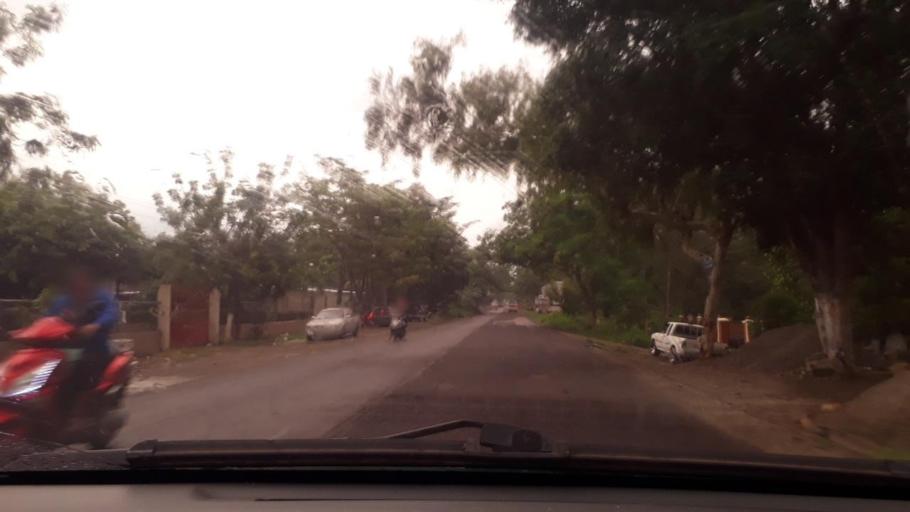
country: GT
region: Jutiapa
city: Jalpatagua
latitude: 14.1425
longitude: -90.0240
